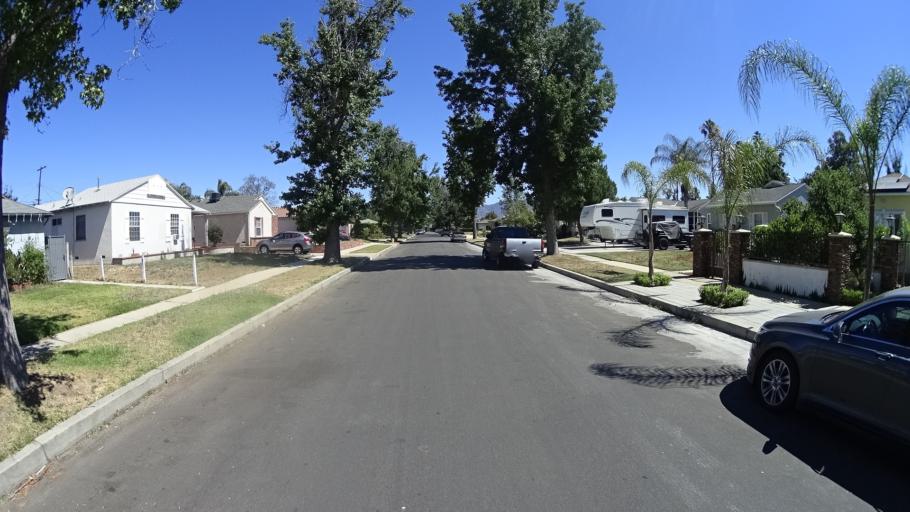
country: US
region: California
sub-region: Los Angeles County
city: San Fernando
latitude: 34.2542
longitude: -118.4620
